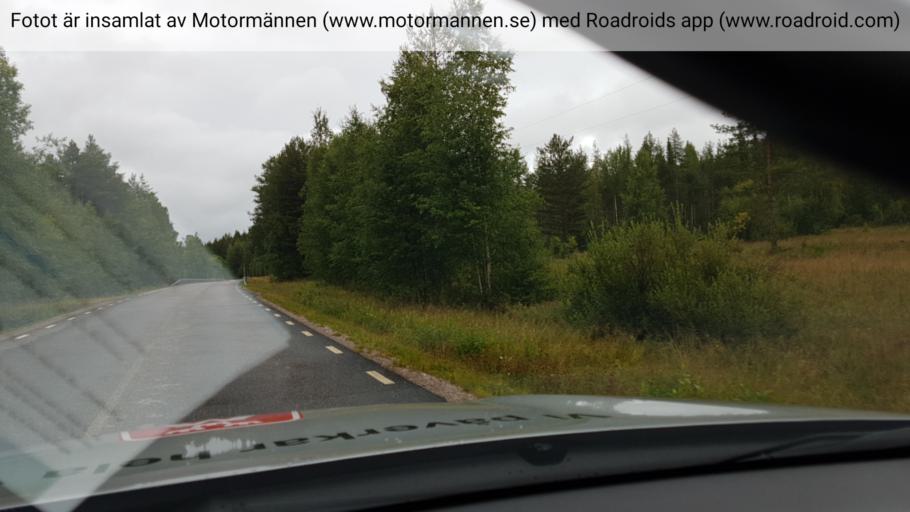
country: SE
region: Norrbotten
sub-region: Gallivare Kommun
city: Gaellivare
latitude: 66.5651
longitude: 20.4908
